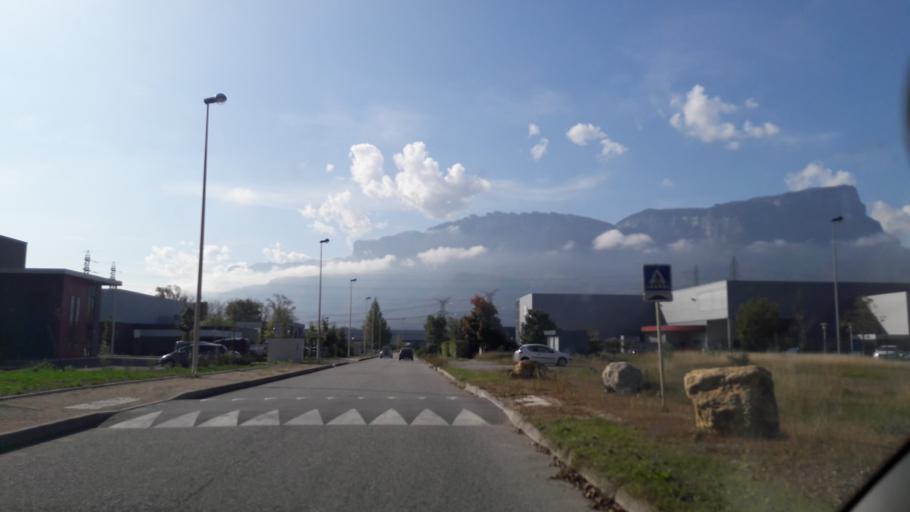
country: FR
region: Rhone-Alpes
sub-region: Departement de la Savoie
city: Montmelian
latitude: 45.4753
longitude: 6.0308
